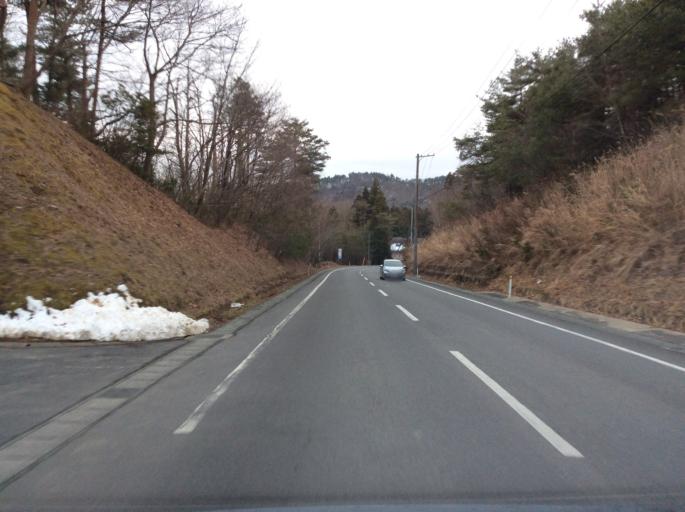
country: JP
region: Fukushima
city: Iwaki
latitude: 37.1608
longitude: 140.9449
